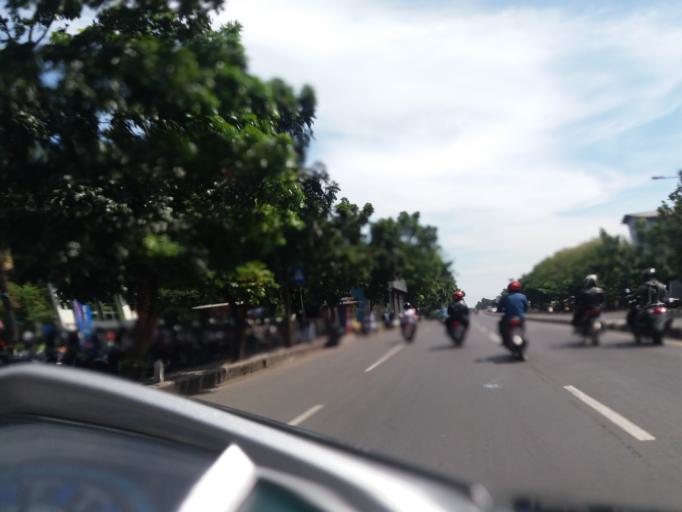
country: ID
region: West Java
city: Bandung
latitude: -6.9496
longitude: 107.6247
